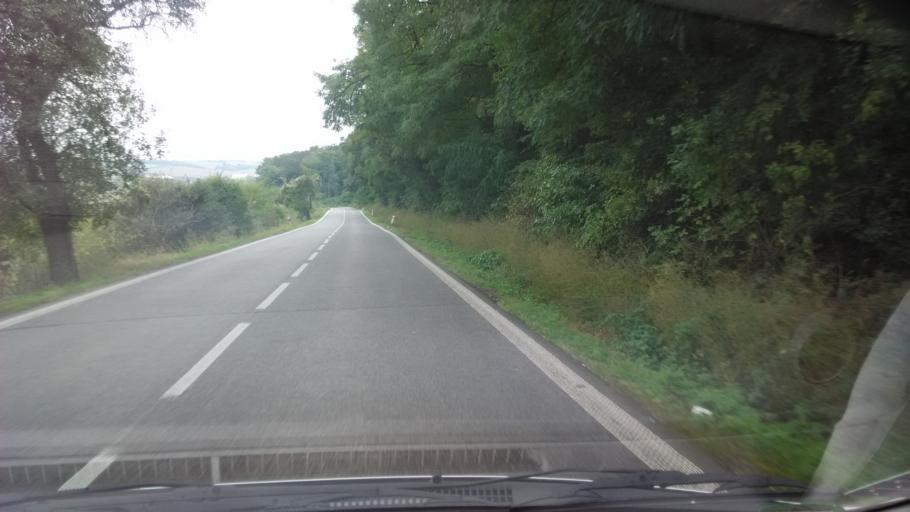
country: SK
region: Banskobystricky
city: Dudince
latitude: 48.1176
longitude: 18.8663
